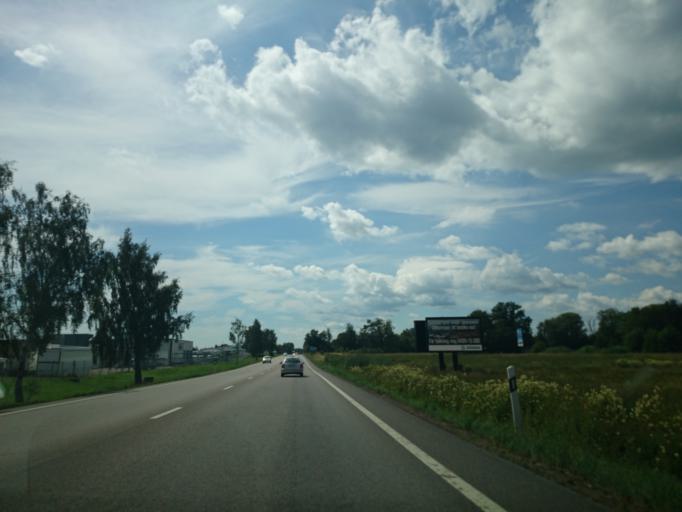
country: SE
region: Kalmar
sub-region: Monsteras Kommun
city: Moensteras
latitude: 57.0396
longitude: 16.4352
